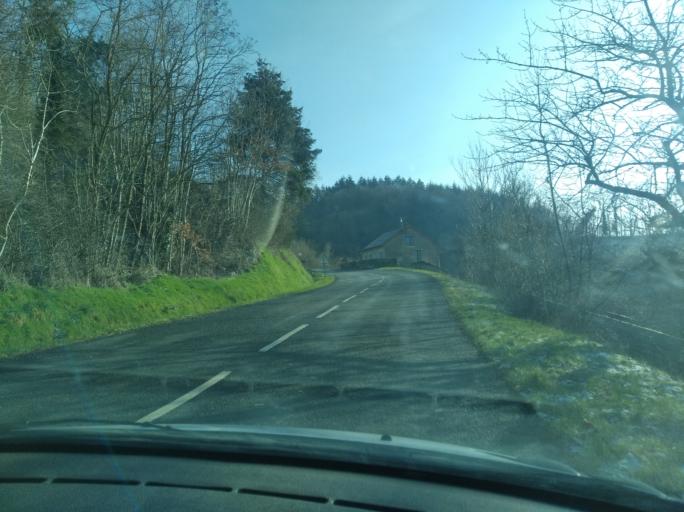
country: FR
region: Auvergne
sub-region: Departement de l'Allier
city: Le Mayet-de-Montagne
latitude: 46.1543
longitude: 3.7334
